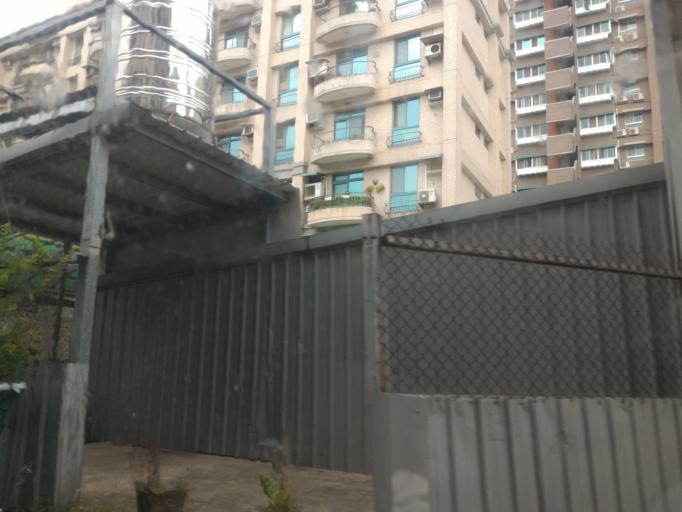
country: TW
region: Taipei
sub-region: Taipei
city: Banqiao
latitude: 25.0866
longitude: 121.4589
